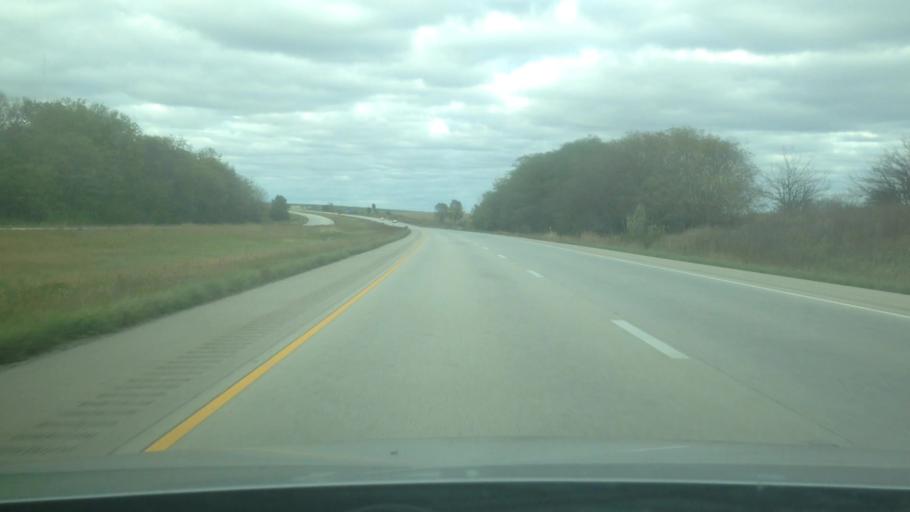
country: US
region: Illinois
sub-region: Macon County
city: Forsyth
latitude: 39.9291
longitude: -88.8454
